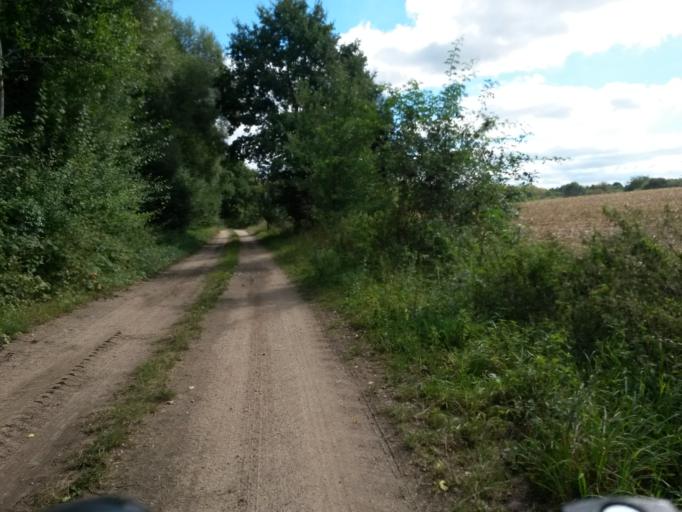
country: DE
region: Brandenburg
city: Mittenwalde
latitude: 53.2086
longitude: 13.5847
